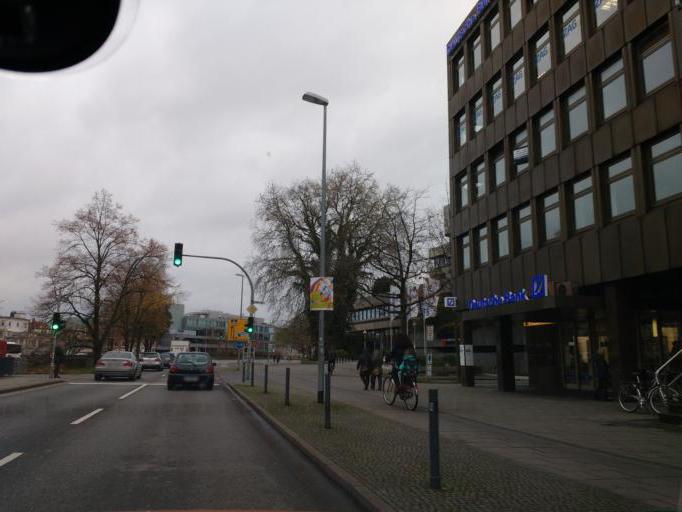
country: DE
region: Lower Saxony
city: Oldenburg
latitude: 53.1424
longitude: 8.2154
